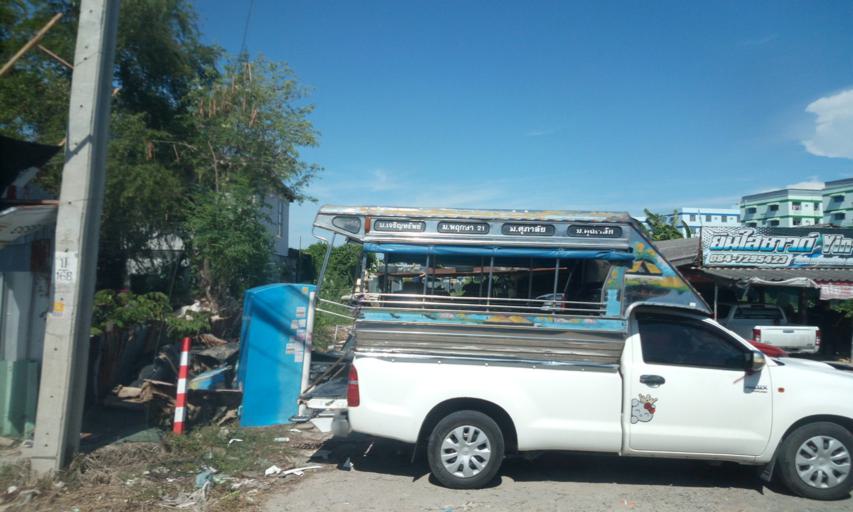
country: TH
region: Samut Prakan
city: Bang Bo District
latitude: 13.5357
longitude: 100.7883
